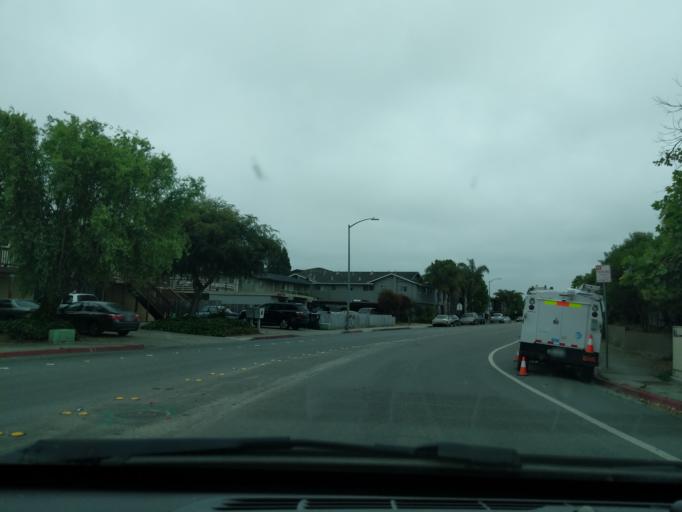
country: US
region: California
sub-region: Santa Cruz County
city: Freedom
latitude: 36.9204
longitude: -121.7726
